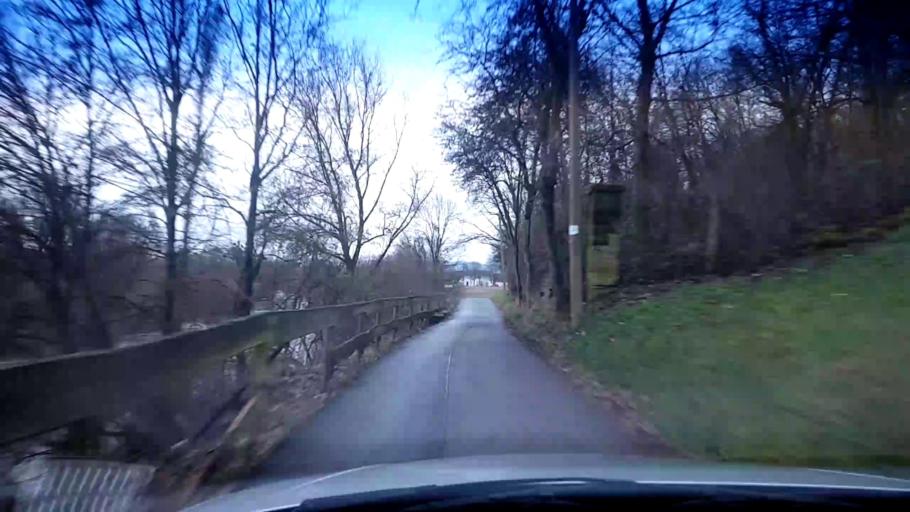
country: DE
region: Bavaria
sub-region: Upper Franconia
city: Hallstadt
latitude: 49.9370
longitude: 10.8653
